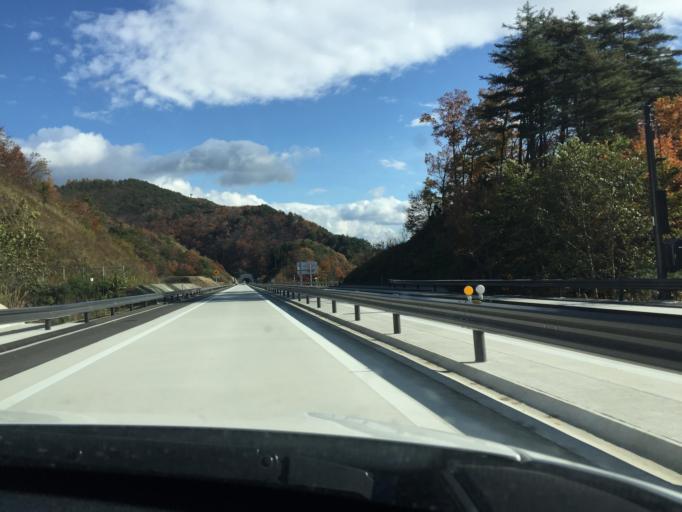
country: JP
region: Fukushima
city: Fukushima-shi
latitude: 37.8370
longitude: 140.3829
